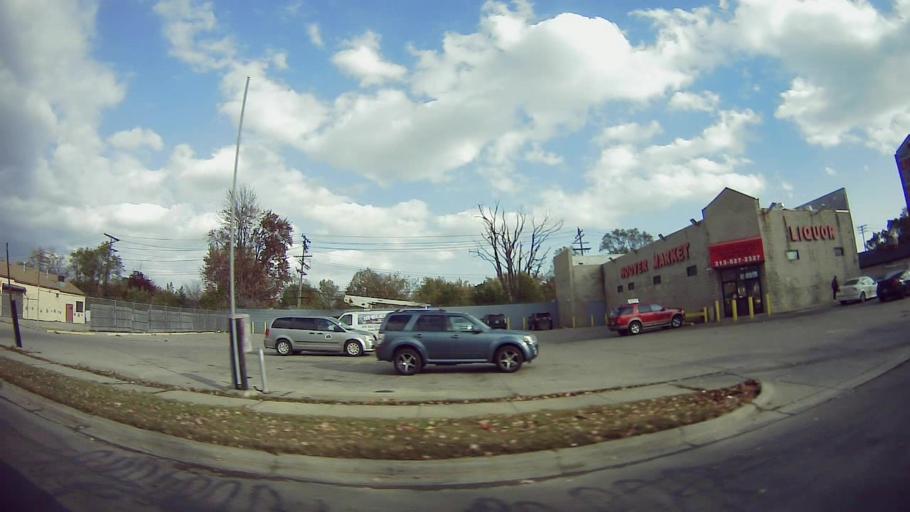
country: US
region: Michigan
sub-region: Macomb County
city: Warren
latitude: 42.4426
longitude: -83.0050
